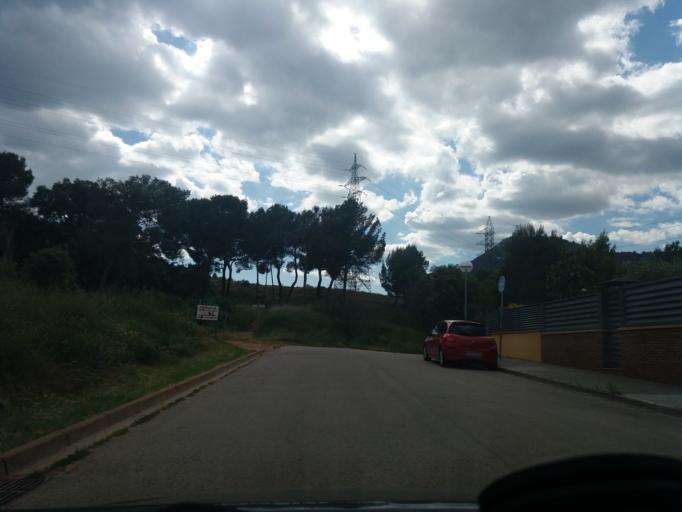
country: ES
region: Catalonia
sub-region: Provincia de Barcelona
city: Sant Joan de Vilatorrada
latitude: 41.7382
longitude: 1.7980
